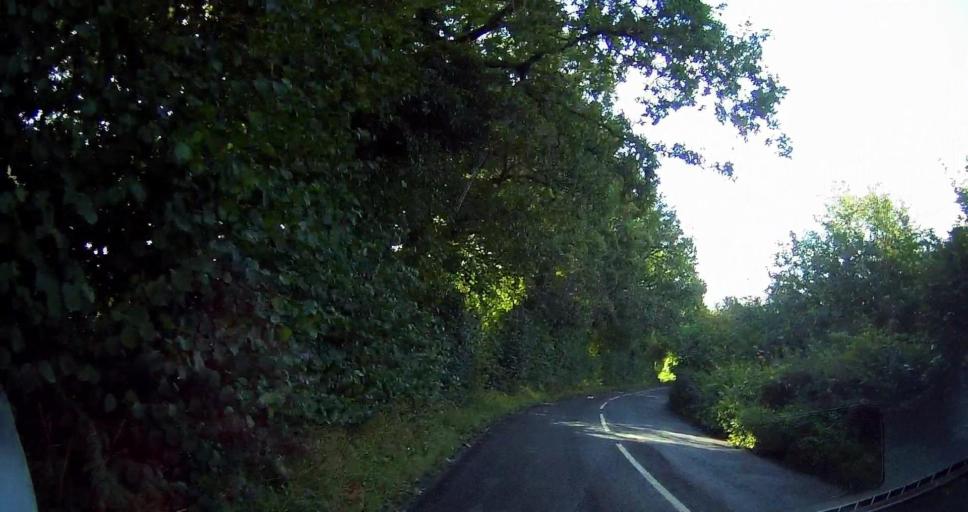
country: GB
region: England
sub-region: Kent
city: Borough Green
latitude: 51.3156
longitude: 0.2806
